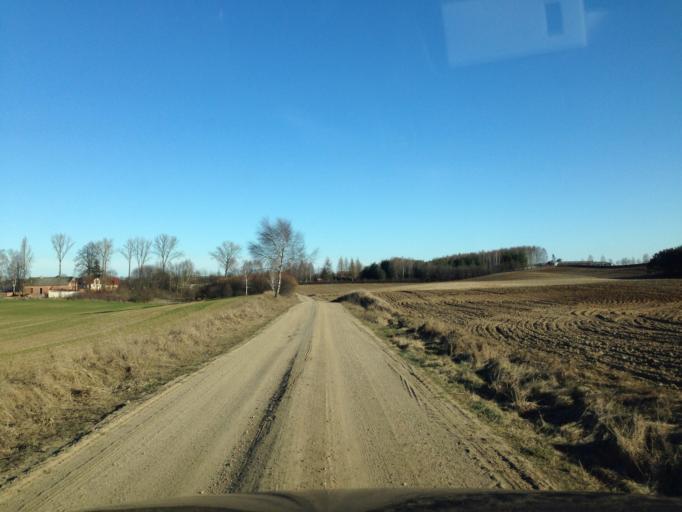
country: PL
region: Kujawsko-Pomorskie
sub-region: Powiat brodnicki
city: Brzozie
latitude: 53.3257
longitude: 19.6590
